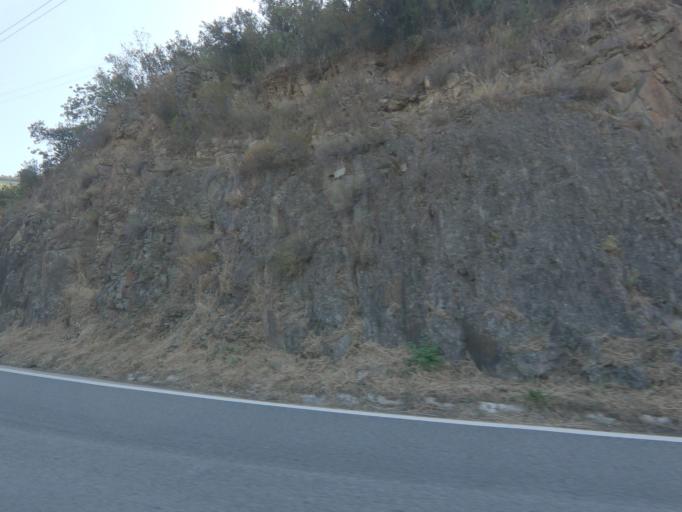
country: PT
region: Viseu
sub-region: Tabuaco
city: Tabuaco
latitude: 41.1471
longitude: -7.5773
